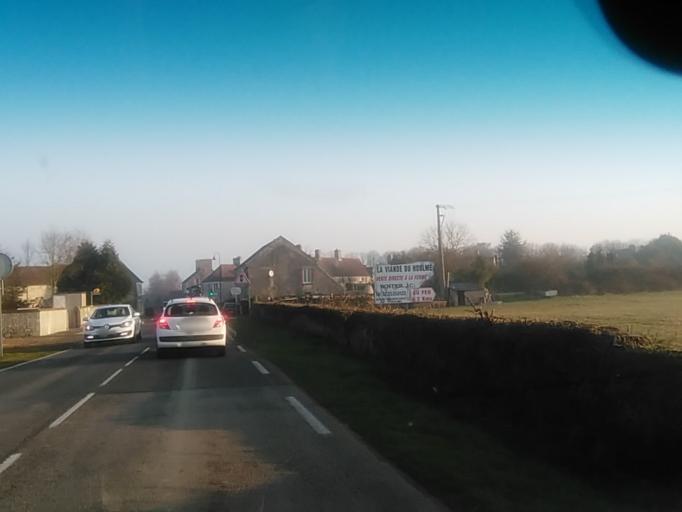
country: FR
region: Lower Normandy
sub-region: Departement de l'Orne
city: Pont-Ecrepin
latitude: 48.8151
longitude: -0.2415
